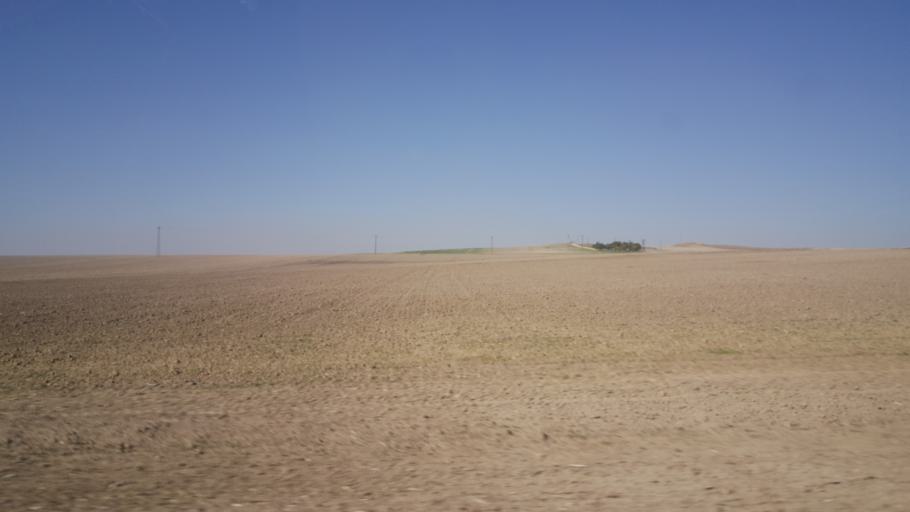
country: TR
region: Konya
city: Celtik
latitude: 39.0656
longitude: 31.8935
